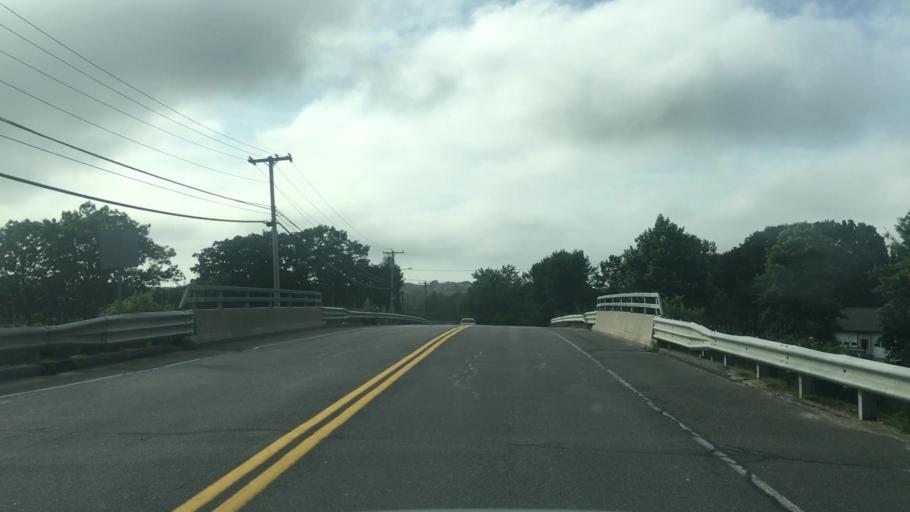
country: US
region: Maine
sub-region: Cumberland County
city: Scarborough
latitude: 43.5779
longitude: -70.3224
